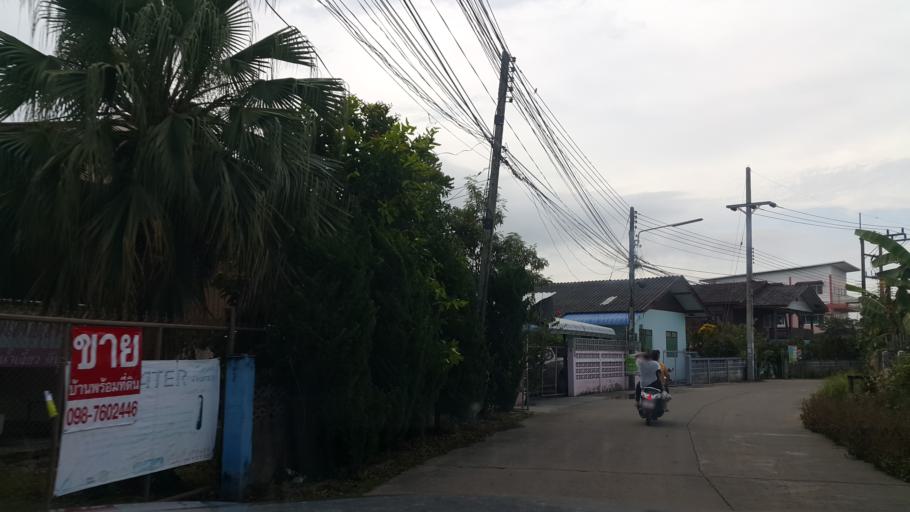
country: TH
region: Chiang Rai
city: Chiang Rai
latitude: 19.9260
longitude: 99.8491
